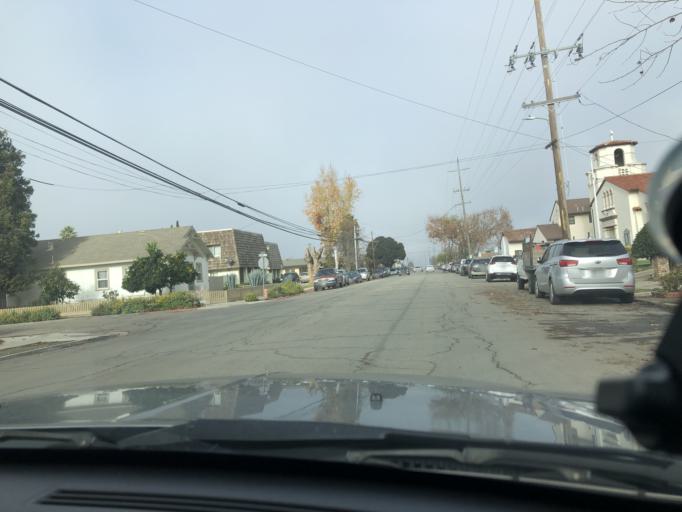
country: US
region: California
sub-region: Monterey County
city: King City
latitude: 36.2167
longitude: -121.1294
